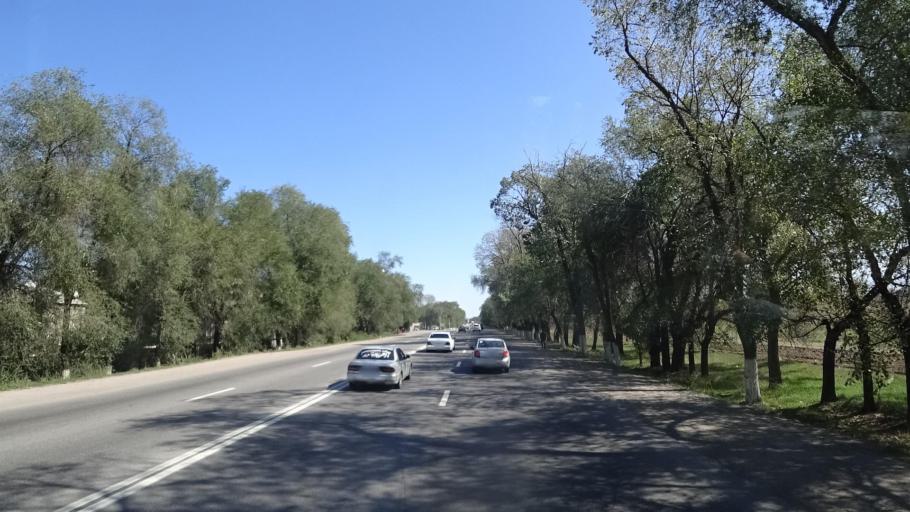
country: KZ
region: Almaty Oblysy
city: Talghar
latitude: 43.3960
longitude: 77.1472
